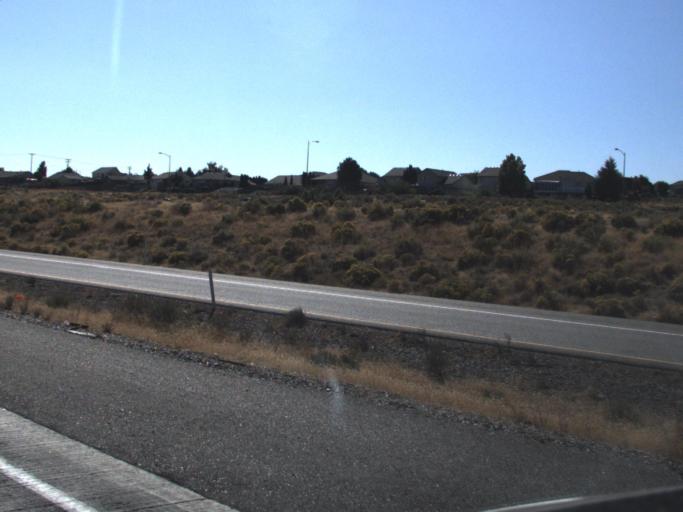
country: US
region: Washington
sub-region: Franklin County
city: West Pasco
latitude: 46.2365
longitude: -119.2412
